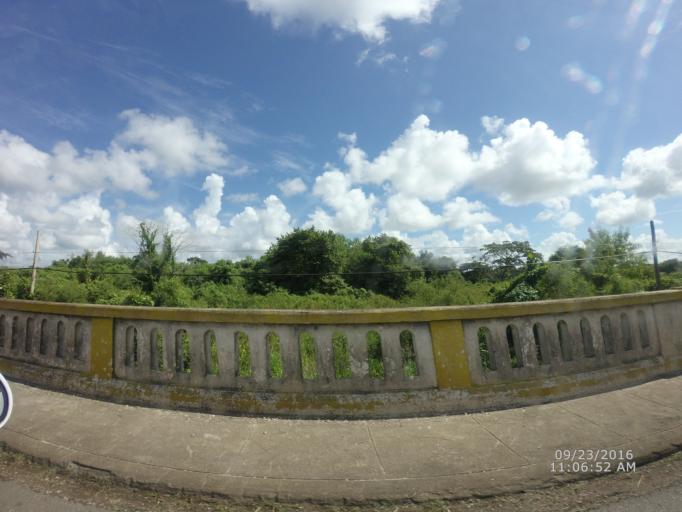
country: CU
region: Mayabeque
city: Jamaica
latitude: 23.0130
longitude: -82.2251
